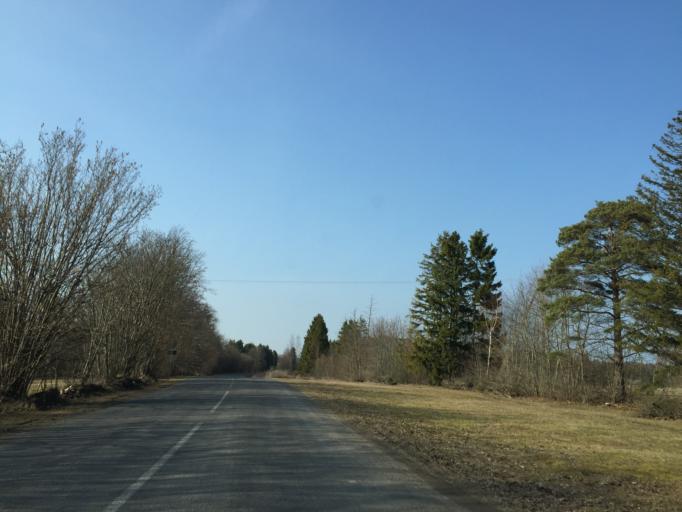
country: EE
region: Saare
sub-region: Orissaare vald
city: Orissaare
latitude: 58.6008
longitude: 23.3186
